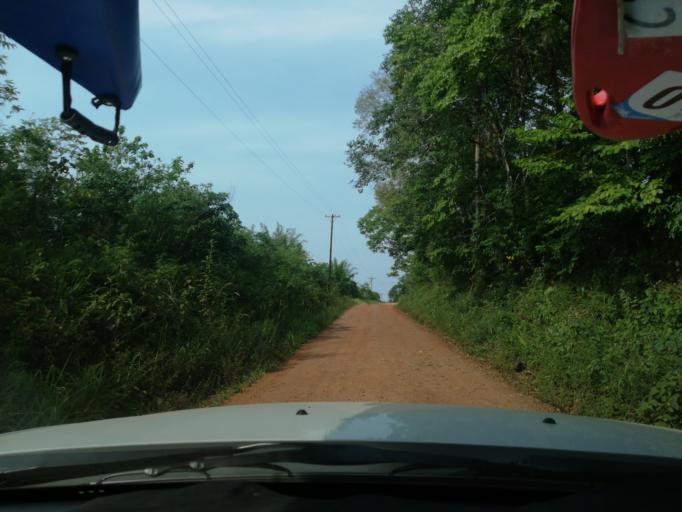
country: AR
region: Misiones
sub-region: Departamento de San Ignacio
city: San Ignacio
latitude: -27.2955
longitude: -55.5700
